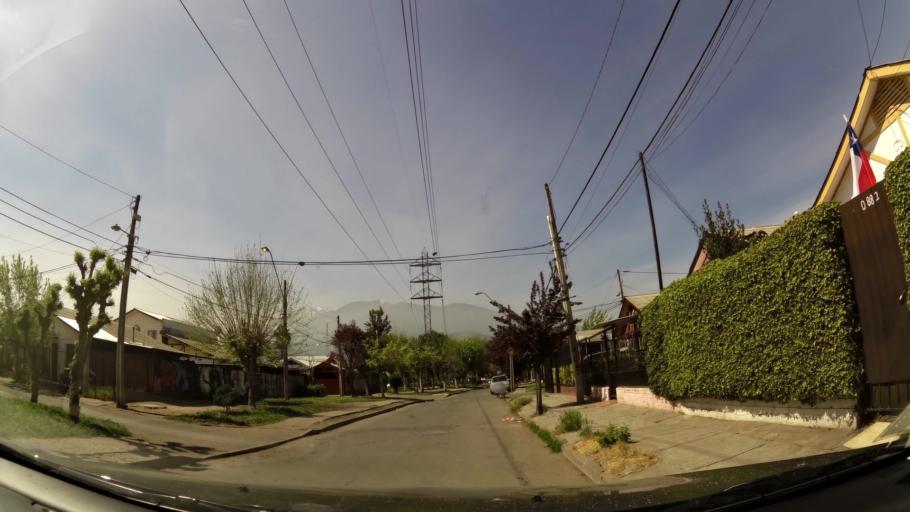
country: CL
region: Santiago Metropolitan
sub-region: Provincia de Cordillera
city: Puente Alto
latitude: -33.5702
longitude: -70.5737
